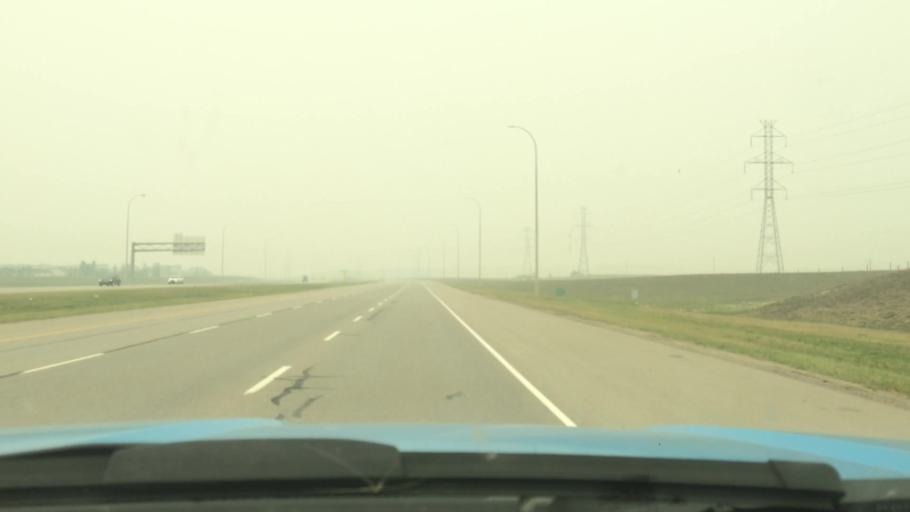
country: CA
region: Alberta
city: Airdrie
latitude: 51.1760
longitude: -114.0362
